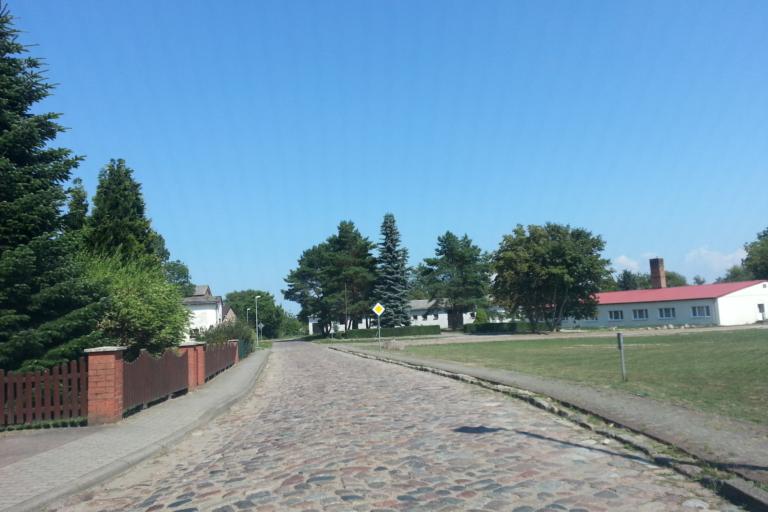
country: DE
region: Mecklenburg-Vorpommern
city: Ferdinandshof
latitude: 53.7014
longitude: 13.8319
